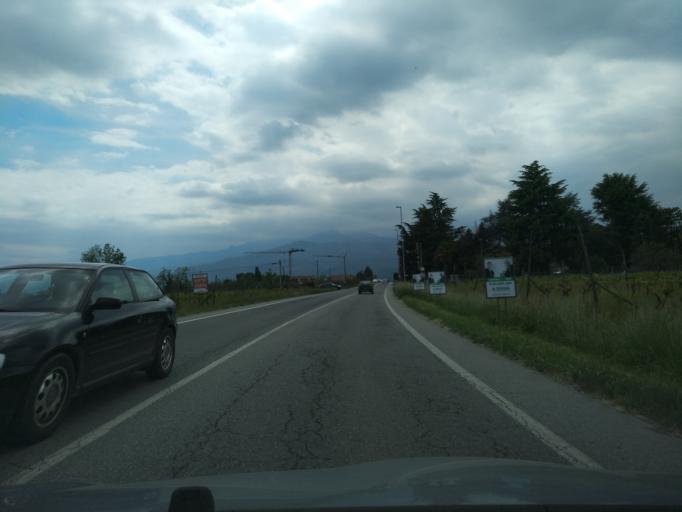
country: IT
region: Piedmont
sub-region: Provincia di Torino
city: Bricherasio
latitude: 44.8231
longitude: 7.3104
